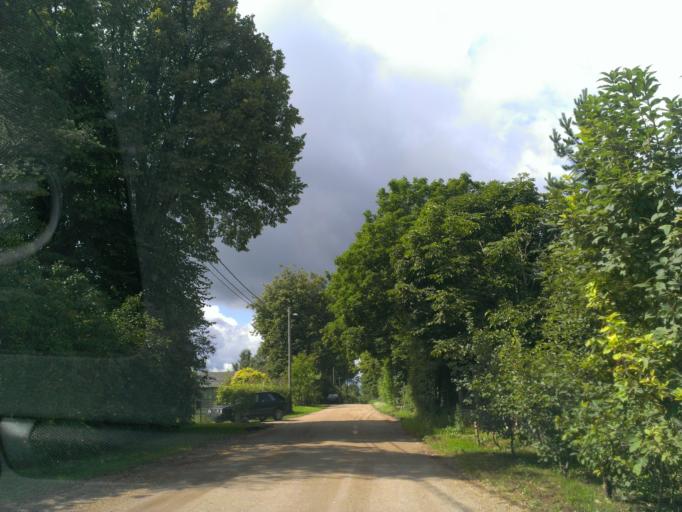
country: LV
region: Sigulda
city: Sigulda
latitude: 57.1476
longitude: 24.8632
